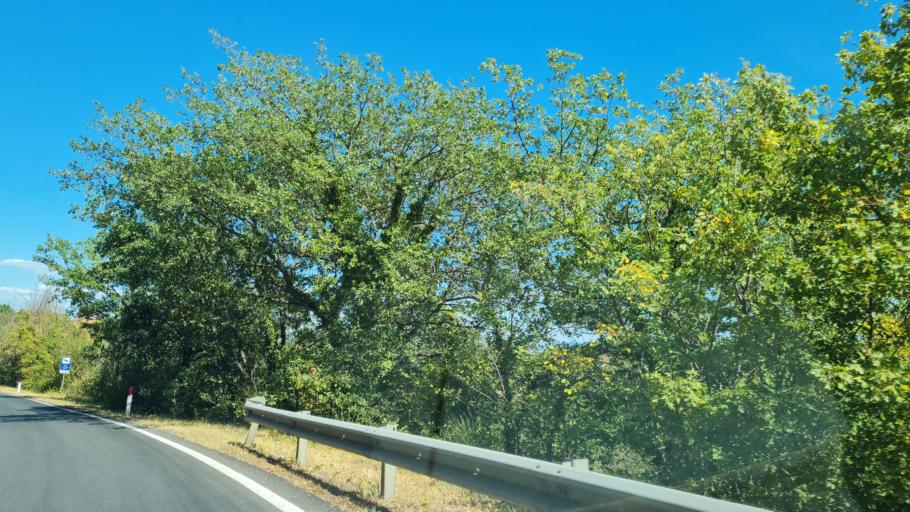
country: IT
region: Tuscany
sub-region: Provincia di Siena
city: Sant'Albino
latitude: 43.0747
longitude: 11.7979
